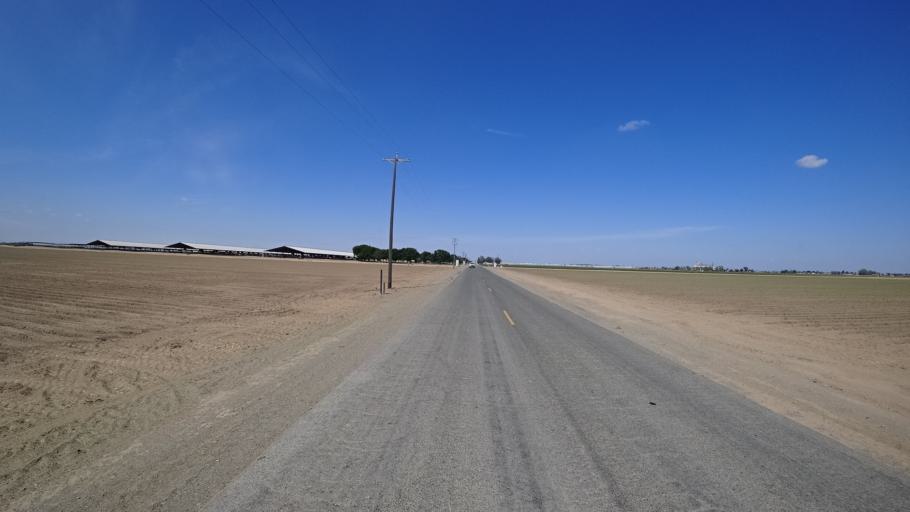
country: US
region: California
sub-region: Kings County
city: Home Garden
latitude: 36.2694
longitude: -119.6215
